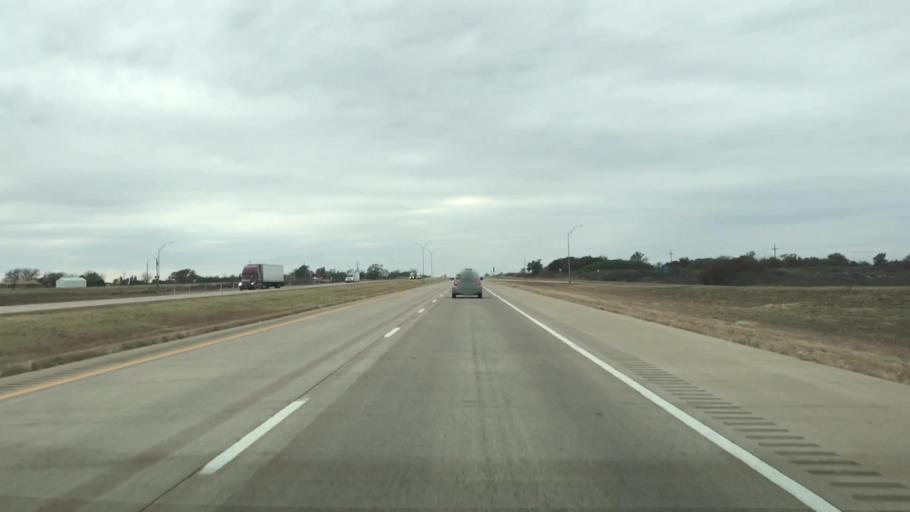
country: US
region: Texas
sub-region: Wheeler County
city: Shamrock
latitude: 35.2270
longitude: -100.1683
